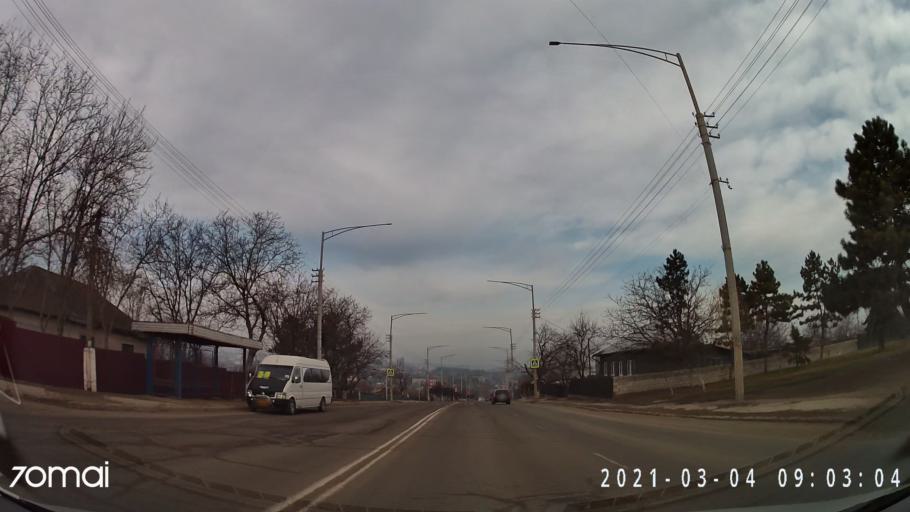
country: MD
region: Balti
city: Balti
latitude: 47.7466
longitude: 27.9478
